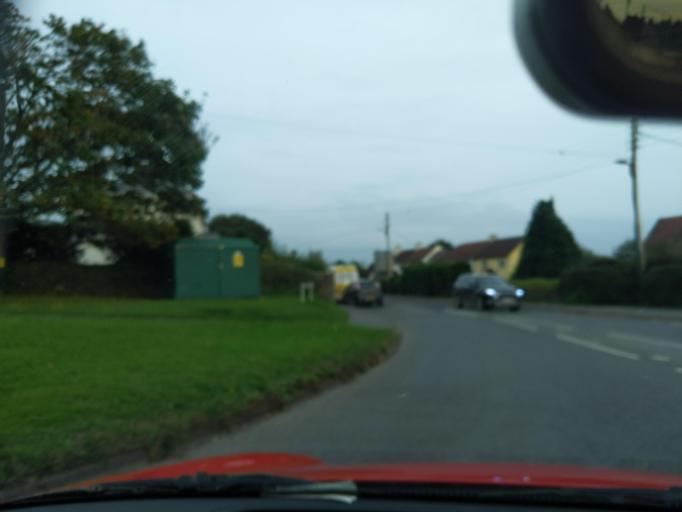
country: GB
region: England
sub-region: Devon
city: Great Torrington
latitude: 50.9546
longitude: -4.1358
